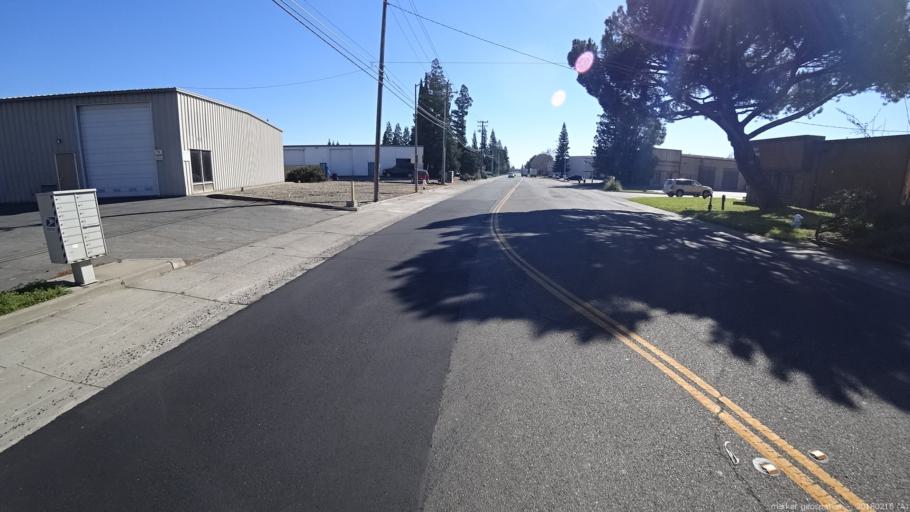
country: US
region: California
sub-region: Sacramento County
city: Gold River
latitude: 38.6193
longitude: -121.2617
